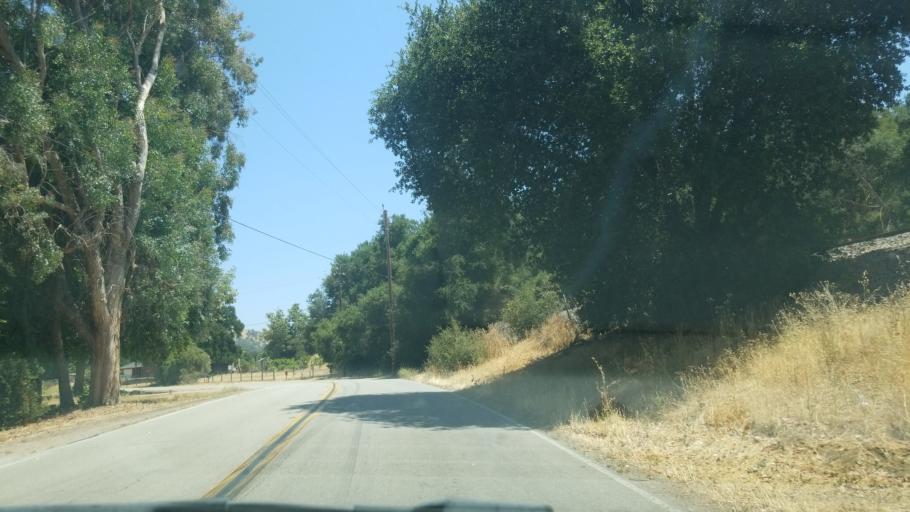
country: US
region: California
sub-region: San Luis Obispo County
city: Atascadero
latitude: 35.4966
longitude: -120.6526
